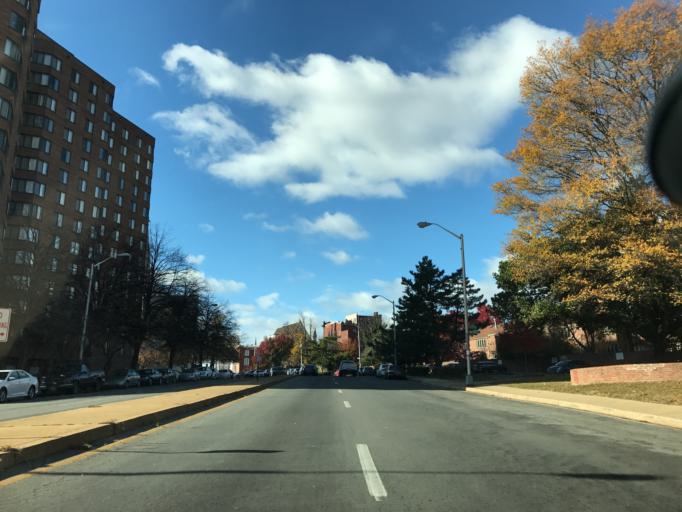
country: US
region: Maryland
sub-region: City of Baltimore
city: Baltimore
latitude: 39.3041
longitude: -76.6230
